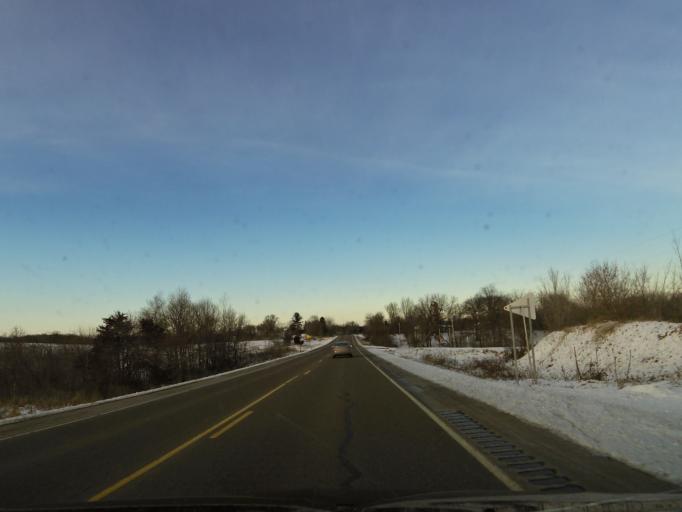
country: US
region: Wisconsin
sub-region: Polk County
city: Osceola
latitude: 45.3537
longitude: -92.7126
